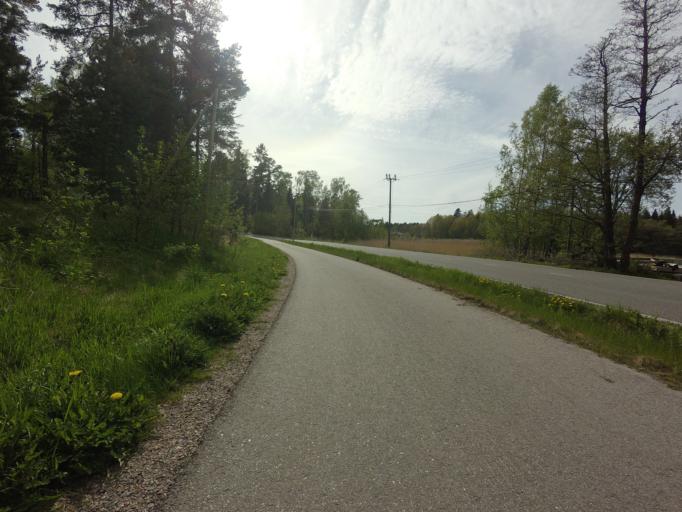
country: FI
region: Uusimaa
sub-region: Helsinki
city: Koukkuniemi
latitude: 60.1281
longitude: 24.7013
